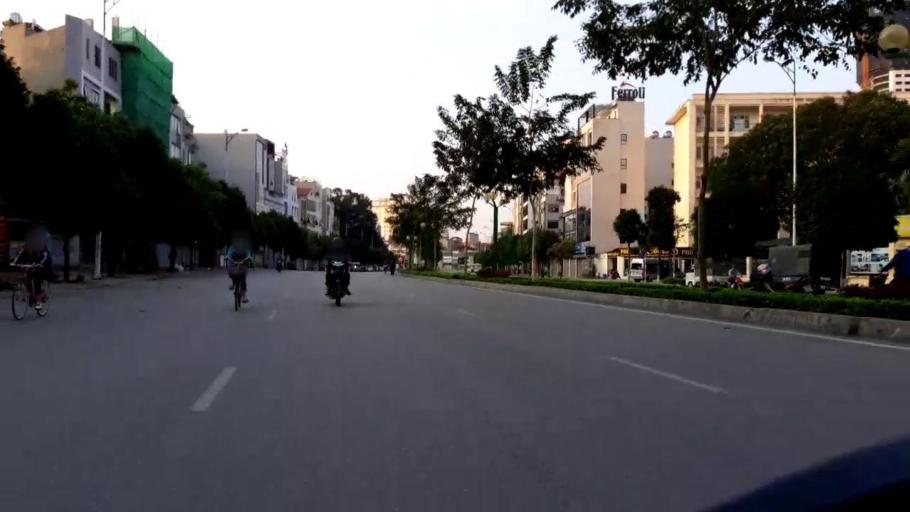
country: VN
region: Ha Noi
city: Cau Giay
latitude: 21.0371
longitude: 105.7979
